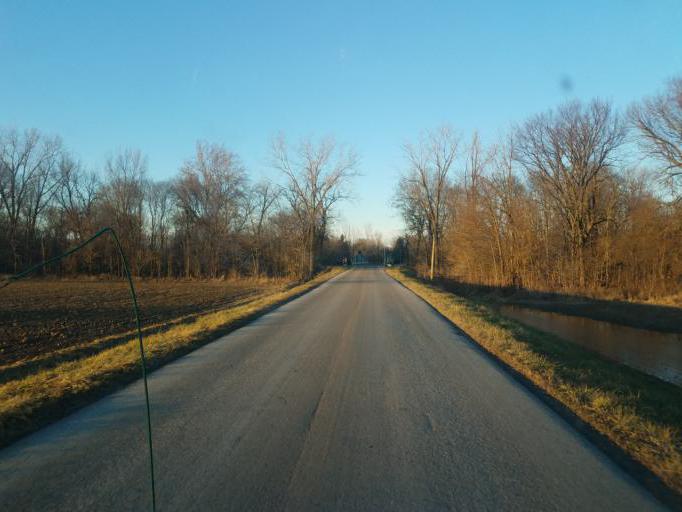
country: US
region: Ohio
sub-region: Hardin County
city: Kenton
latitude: 40.6162
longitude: -83.4698
